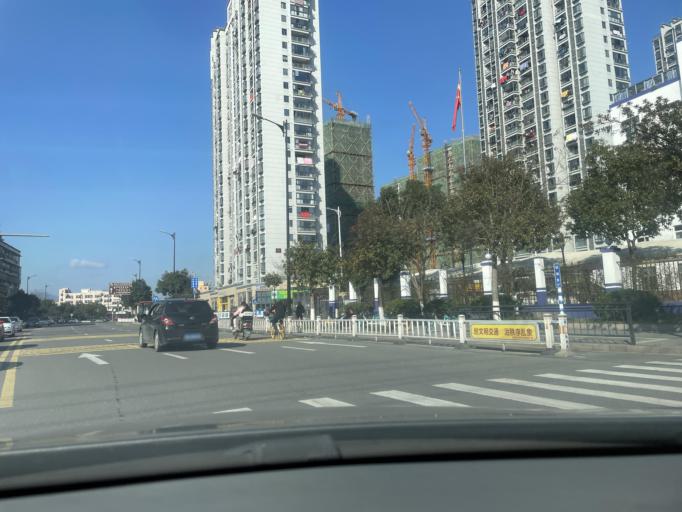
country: CN
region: Zhejiang Sheng
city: Louqiao
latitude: 27.9915
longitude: 120.6136
